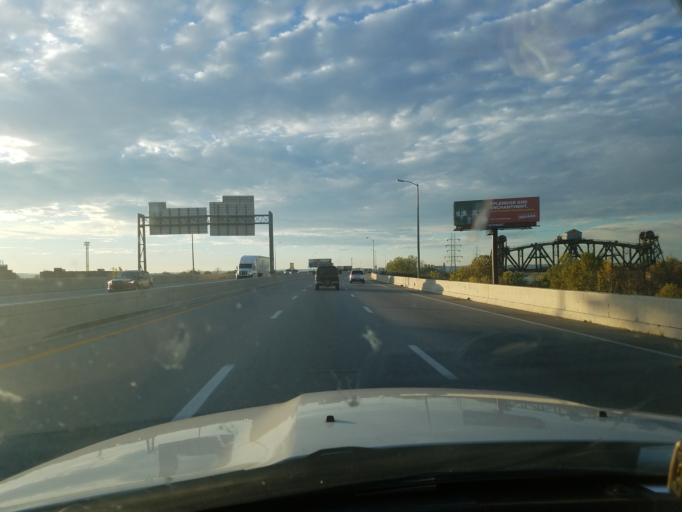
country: US
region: Kentucky
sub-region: Jefferson County
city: Louisville
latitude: 38.2609
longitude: -85.7695
